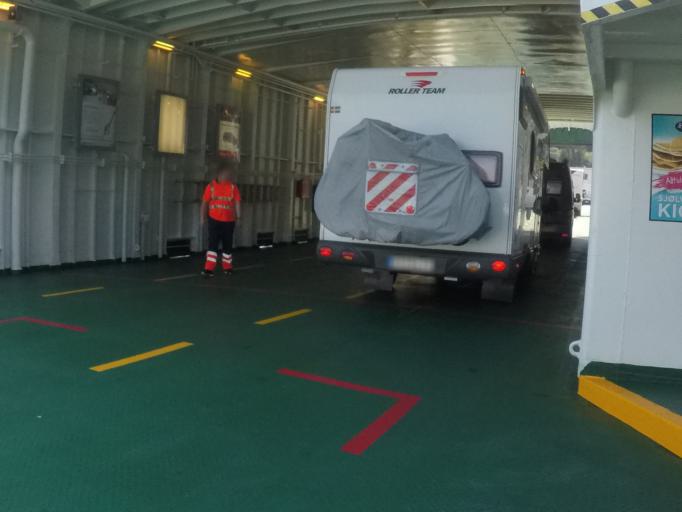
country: NO
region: More og Romsdal
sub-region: Norddal
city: Valldal
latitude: 62.2632
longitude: 7.1709
